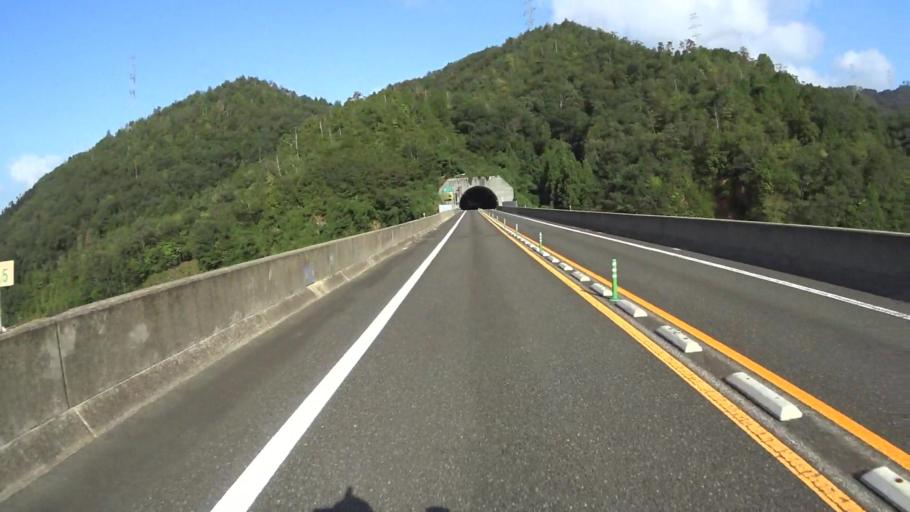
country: JP
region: Kyoto
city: Ayabe
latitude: 35.3701
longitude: 135.2805
